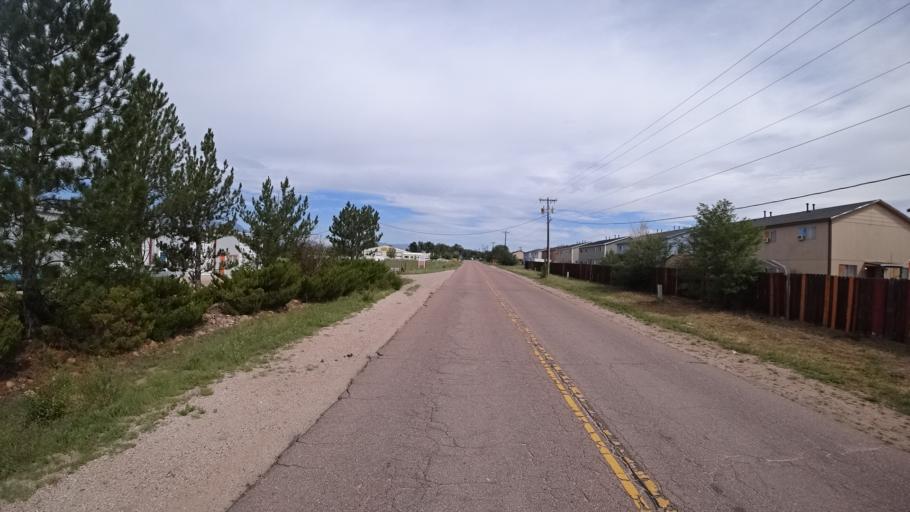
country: US
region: Colorado
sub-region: El Paso County
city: Security-Widefield
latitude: 38.7415
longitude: -104.7392
